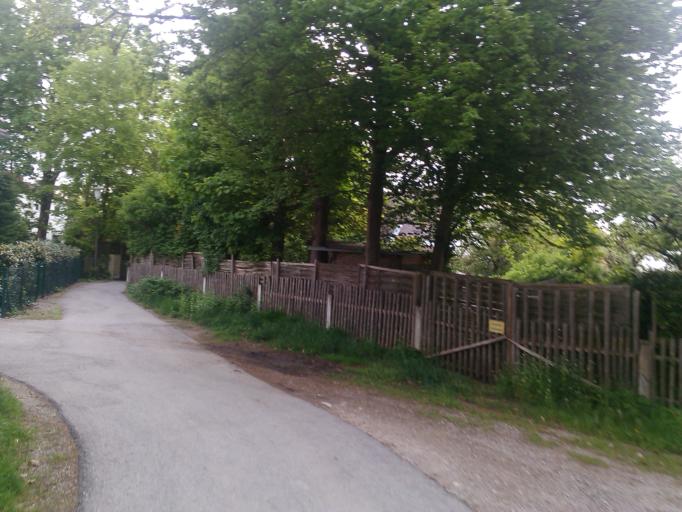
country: DE
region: Bavaria
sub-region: Upper Bavaria
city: Gauting
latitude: 48.0710
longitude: 11.3627
